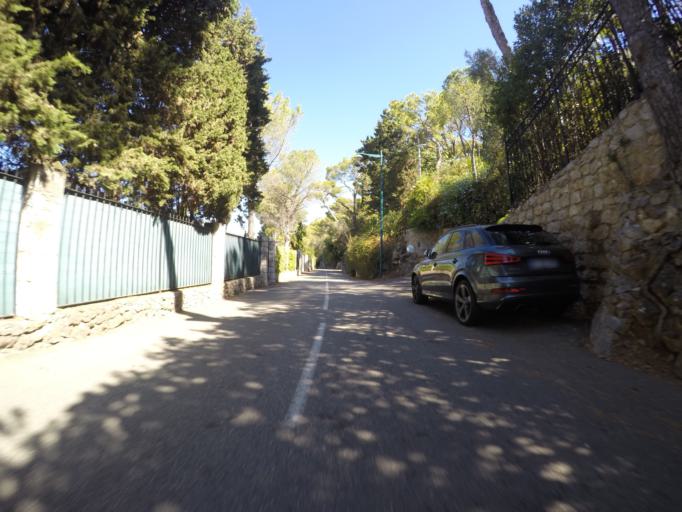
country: FR
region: Provence-Alpes-Cote d'Azur
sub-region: Departement des Alpes-Maritimes
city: Saint-Jean-Cap-Ferrat
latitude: 43.6812
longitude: 7.3263
